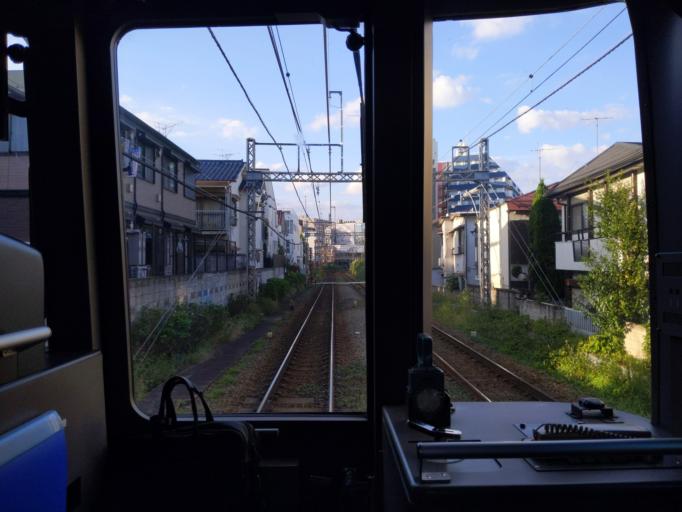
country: JP
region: Tokyo
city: Tokyo
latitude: 35.6657
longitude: 139.6520
